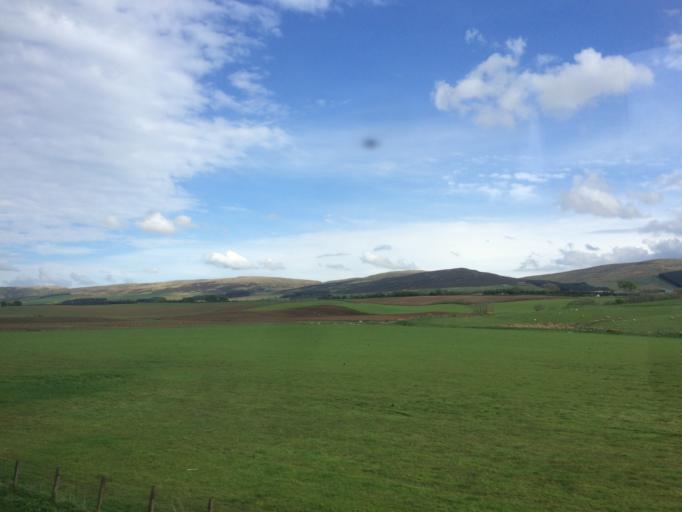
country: GB
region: Scotland
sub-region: Clackmannanshire
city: Alva
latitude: 56.2624
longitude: -3.8138
